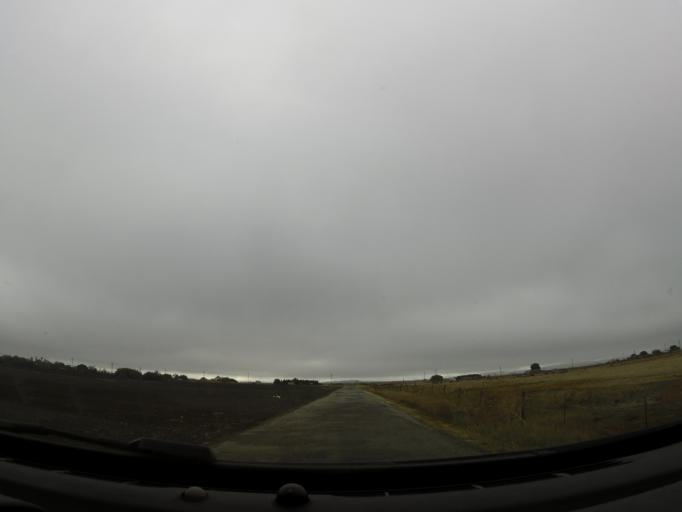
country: US
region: California
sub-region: San Benito County
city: Hollister
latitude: 36.9464
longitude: -121.4490
